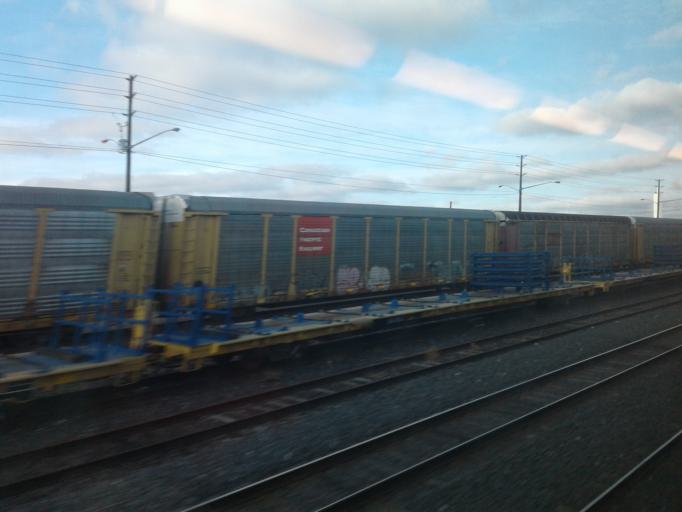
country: CA
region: Ontario
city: Oakville
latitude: 43.4735
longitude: -79.6668
